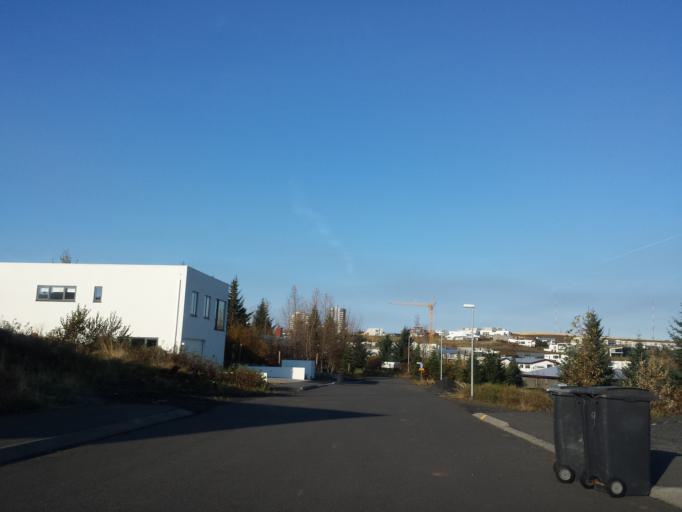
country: IS
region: Capital Region
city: Reykjavik
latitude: 64.0813
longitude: -21.8061
